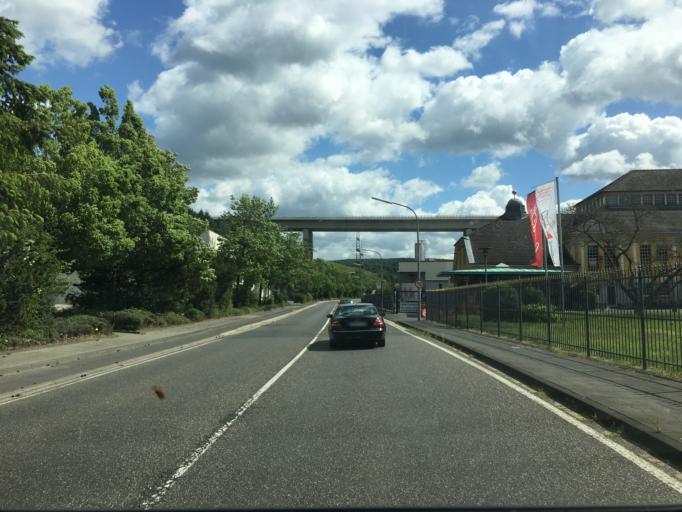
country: DE
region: Rheinland-Pfalz
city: Bad Neuenahr-Ahrweiler
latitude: 50.5477
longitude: 7.1525
